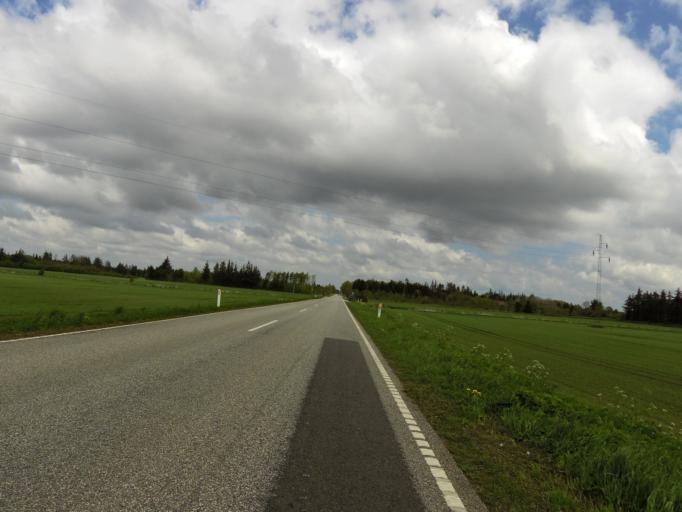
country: DK
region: South Denmark
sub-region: Haderslev Kommune
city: Gram
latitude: 55.2548
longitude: 8.9848
